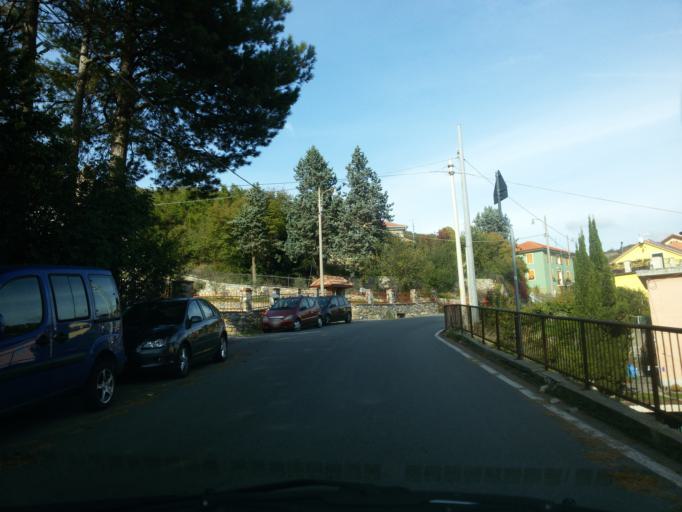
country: IT
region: Liguria
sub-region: Provincia di Genova
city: Piccarello
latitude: 44.4659
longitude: 8.9621
